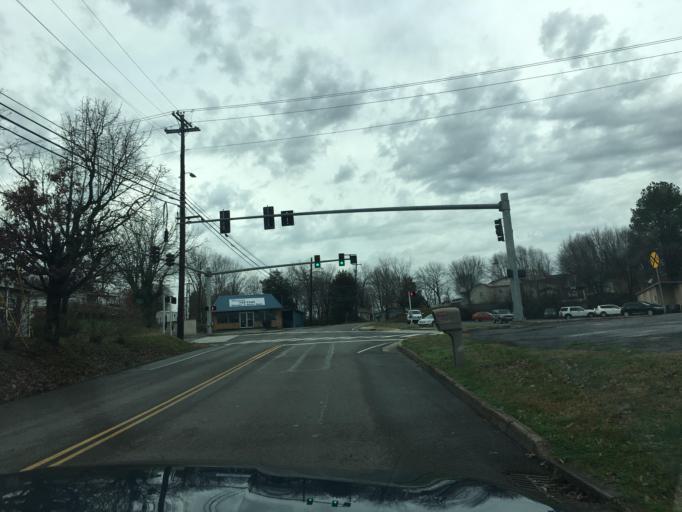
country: US
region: Tennessee
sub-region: McMinn County
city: Athens
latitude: 35.4554
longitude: -84.6039
